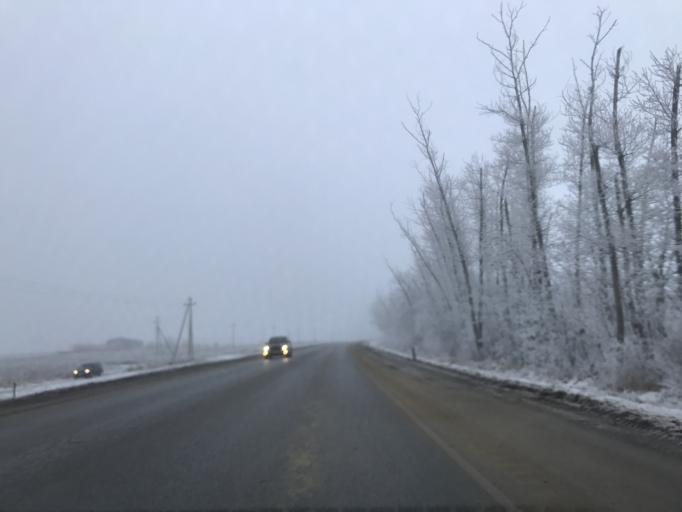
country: RU
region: Rostov
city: Temernik
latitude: 47.3770
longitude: 39.8047
